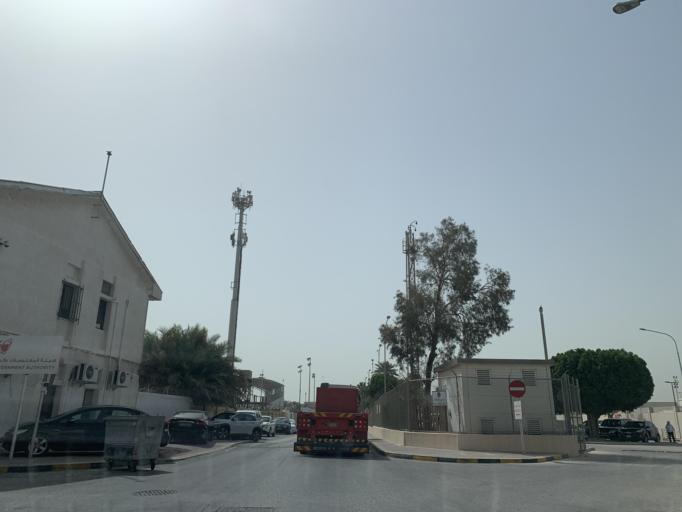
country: BH
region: Manama
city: Manama
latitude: 26.2089
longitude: 50.6052
